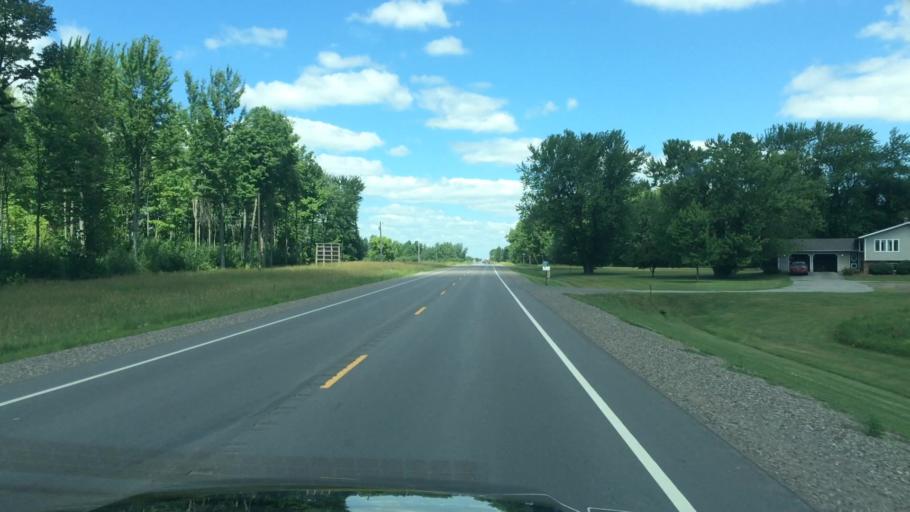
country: US
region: Wisconsin
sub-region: Clark County
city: Abbotsford
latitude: 45.0236
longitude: -90.3151
